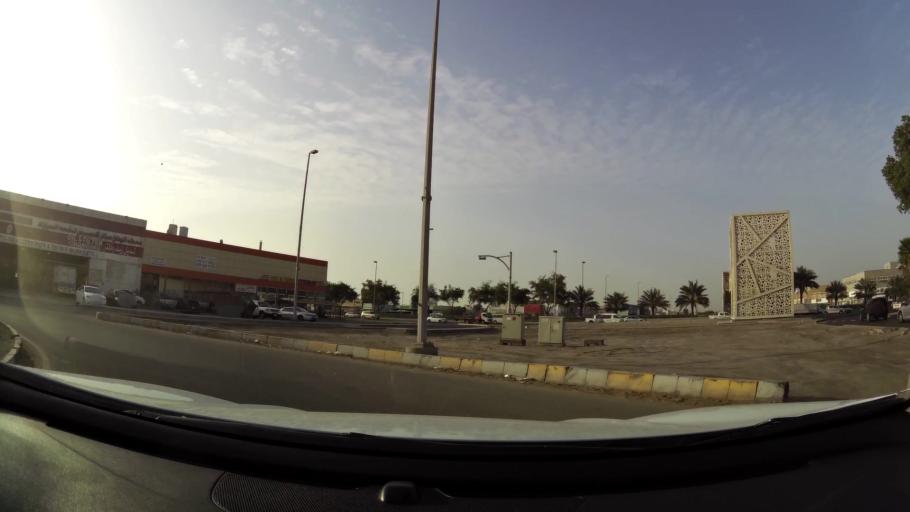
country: AE
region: Abu Dhabi
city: Abu Dhabi
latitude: 24.3726
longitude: 54.5160
